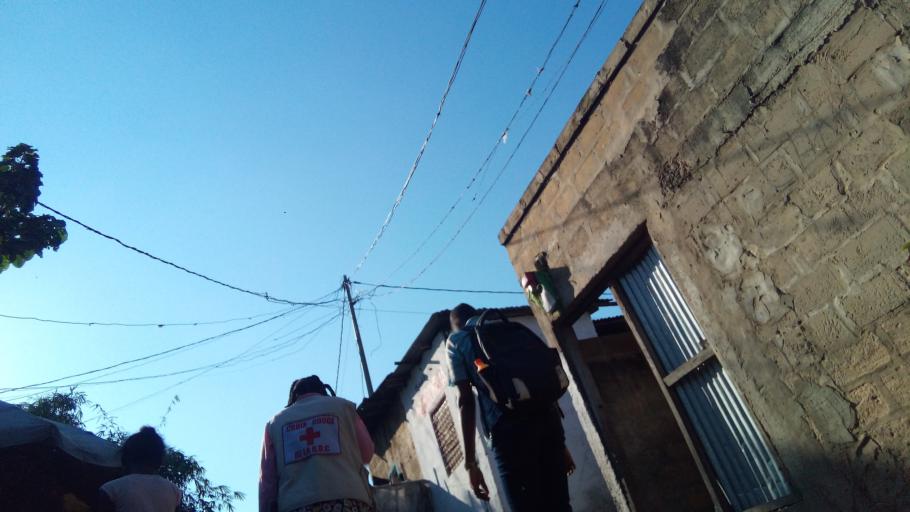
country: CD
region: Kinshasa
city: Kinshasa
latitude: -4.3699
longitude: 15.2773
